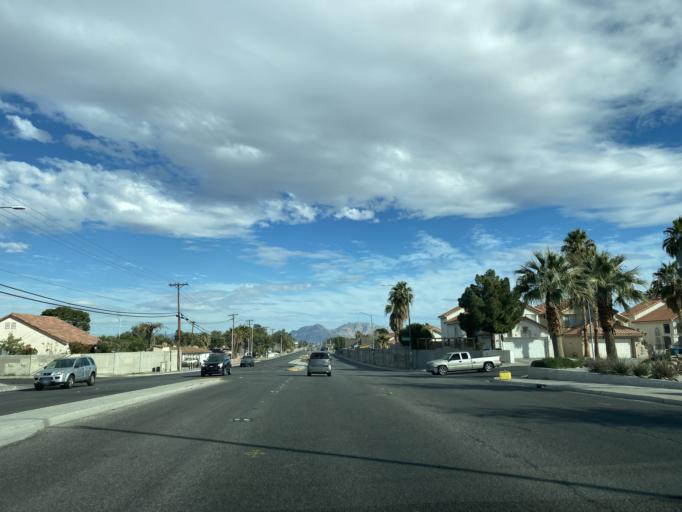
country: US
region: Nevada
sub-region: Clark County
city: Las Vegas
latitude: 36.1885
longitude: -115.1753
